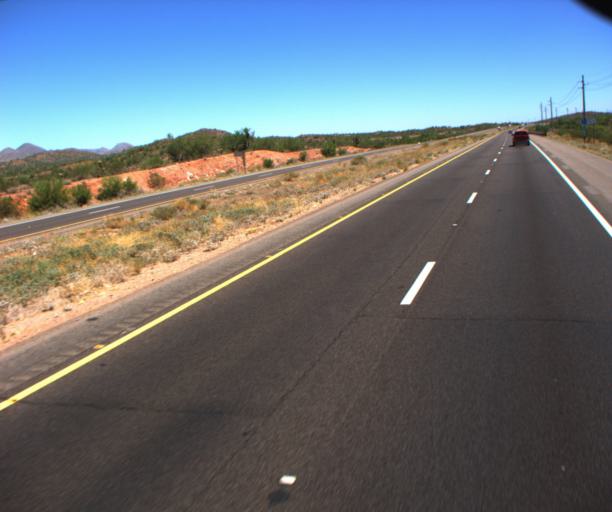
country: US
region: Arizona
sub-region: Maricopa County
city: Fountain Hills
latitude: 33.5437
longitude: -111.7236
